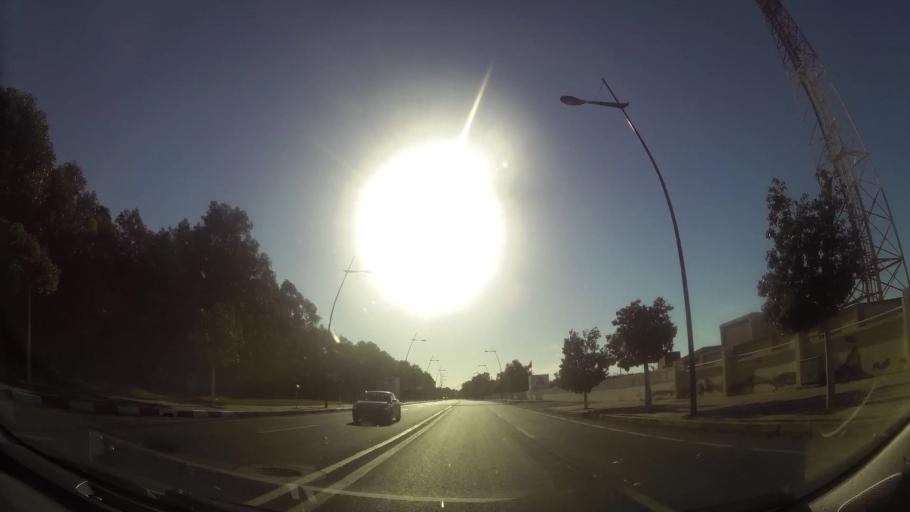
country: MA
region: Oriental
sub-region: Berkane-Taourirt
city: Madagh
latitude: 35.0896
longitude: -2.2449
